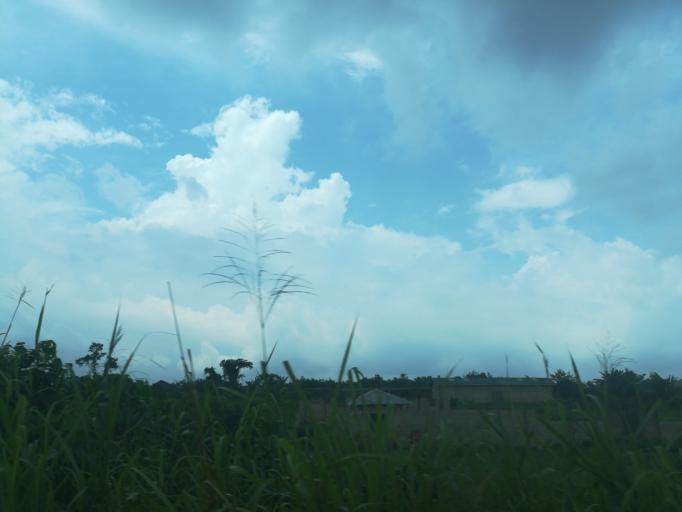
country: NG
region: Lagos
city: Ikorodu
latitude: 6.6633
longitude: 3.6285
